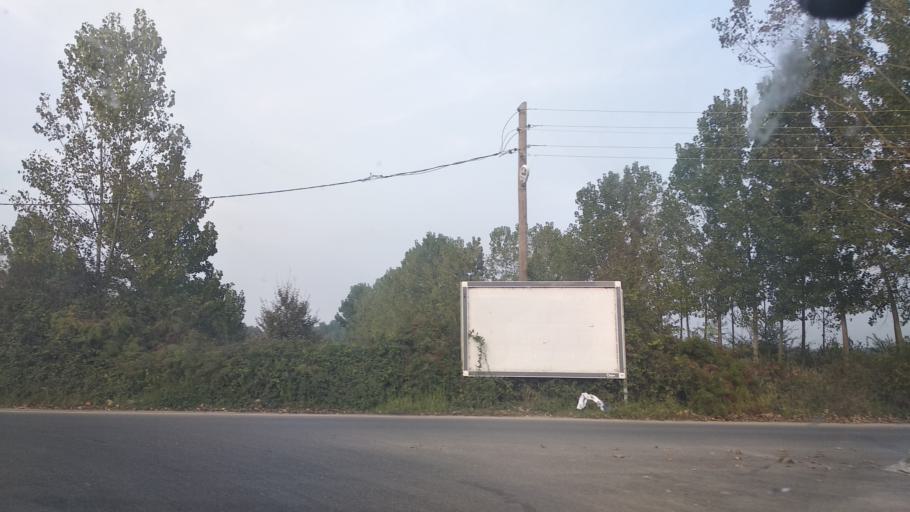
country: TR
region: Duzce
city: Duzce
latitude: 40.8205
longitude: 31.1777
